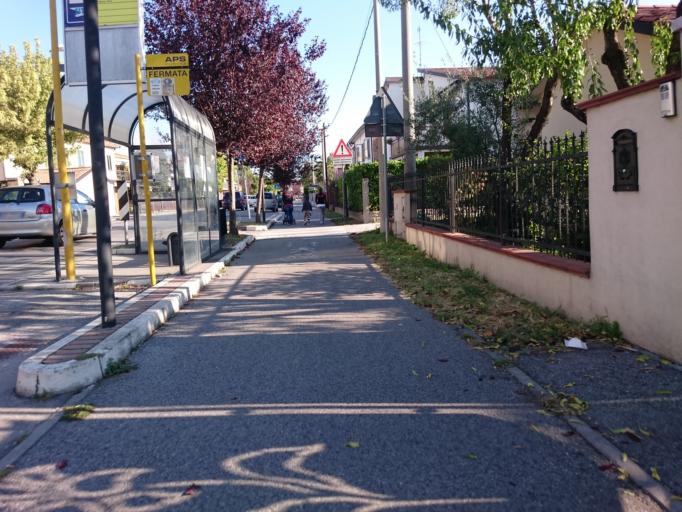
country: IT
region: Veneto
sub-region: Provincia di Padova
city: Masera di Padova
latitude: 45.3375
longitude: 11.8660
